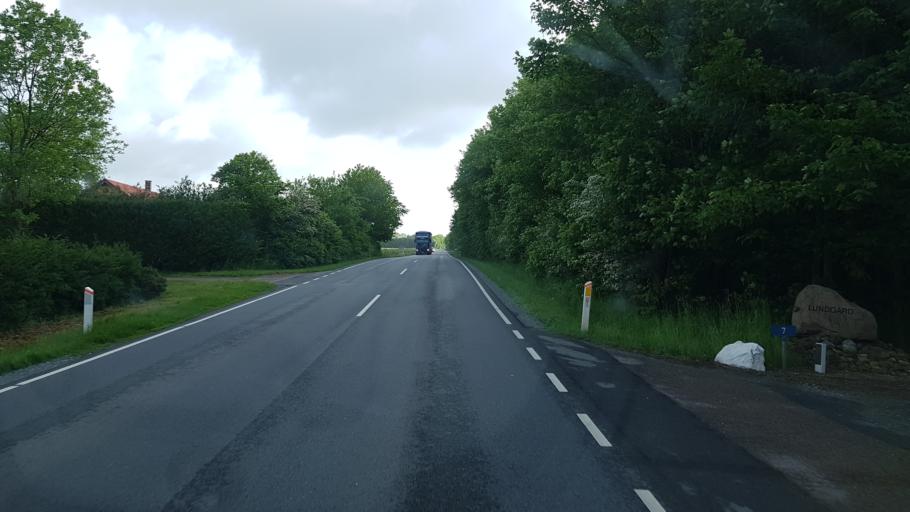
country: DK
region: South Denmark
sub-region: Vejen Kommune
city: Vejen
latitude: 55.4616
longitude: 9.1687
